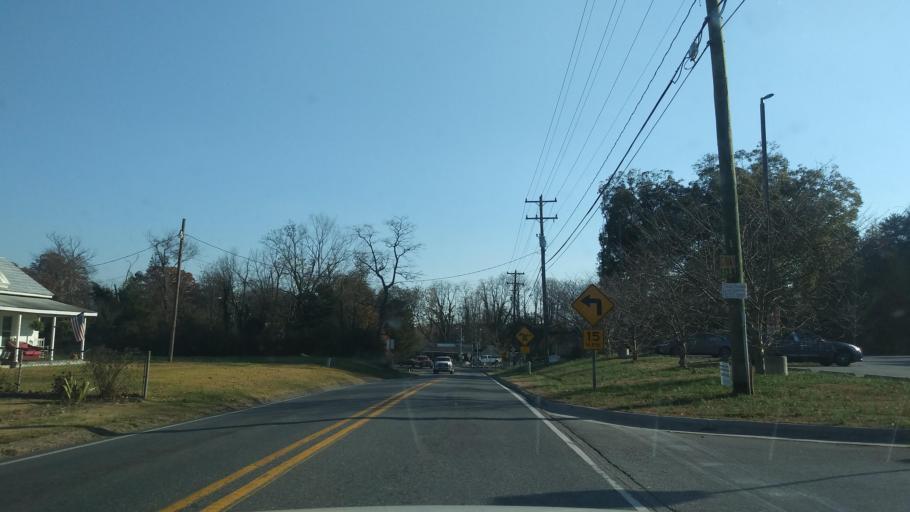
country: US
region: North Carolina
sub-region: Guilford County
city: McLeansville
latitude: 36.2138
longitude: -79.7141
